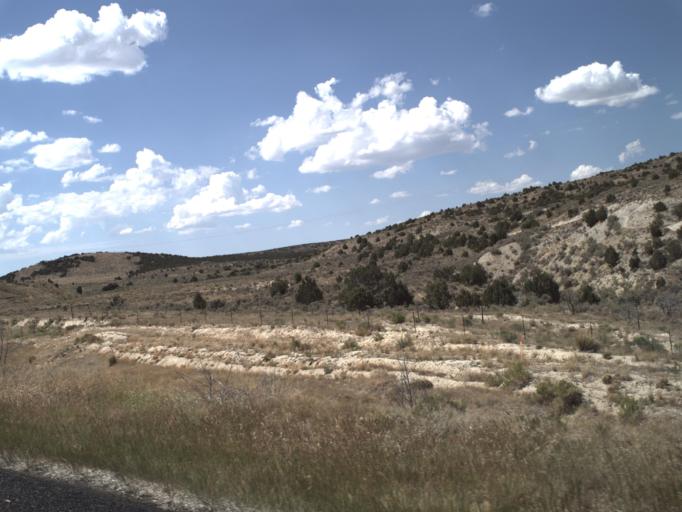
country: US
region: Idaho
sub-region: Minidoka County
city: Rupert
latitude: 41.9724
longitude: -113.1504
